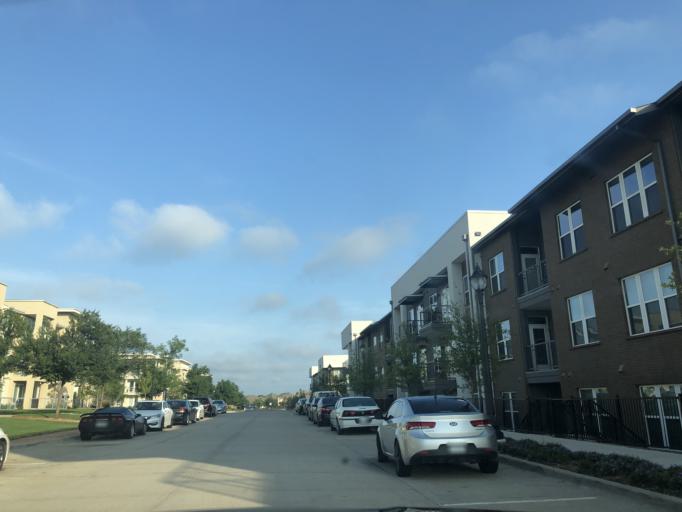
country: US
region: Texas
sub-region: Tarrant County
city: Euless
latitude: 32.8411
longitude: -97.0664
